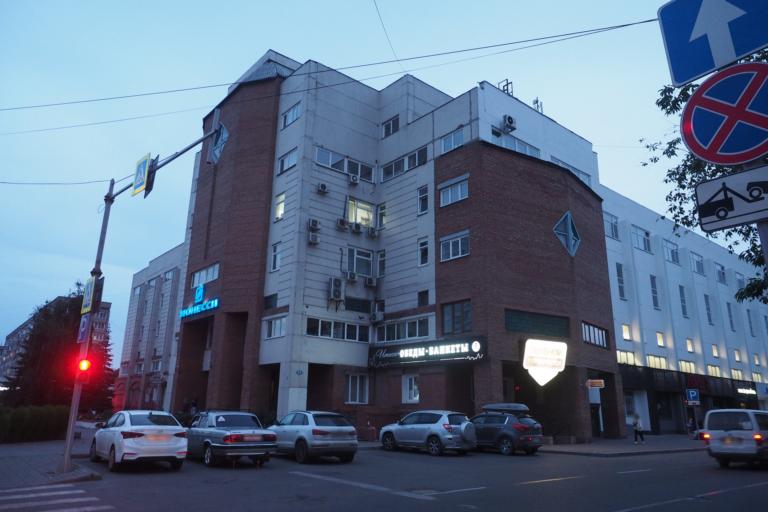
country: RU
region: Krasnoyarskiy
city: Krasnoyarsk
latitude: 56.0107
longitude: 92.8765
